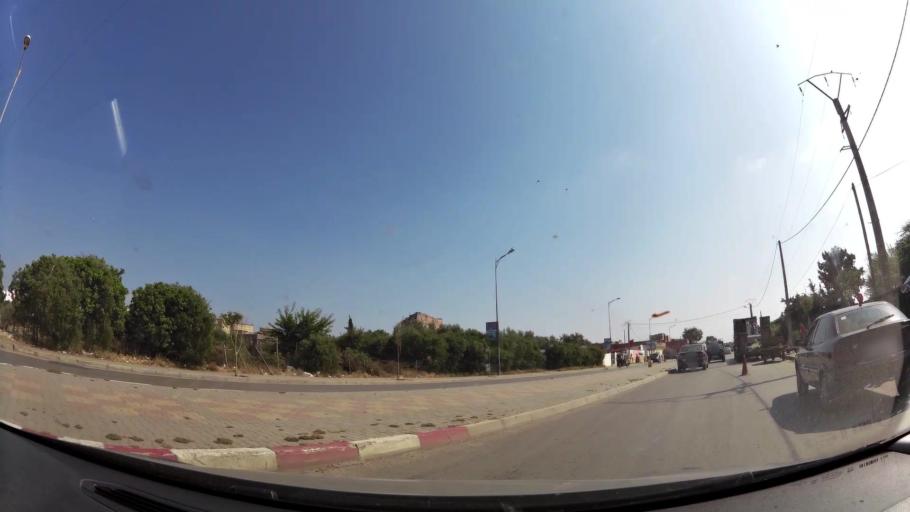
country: MA
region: Rabat-Sale-Zemmour-Zaer
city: Sale
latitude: 34.0707
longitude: -6.7584
